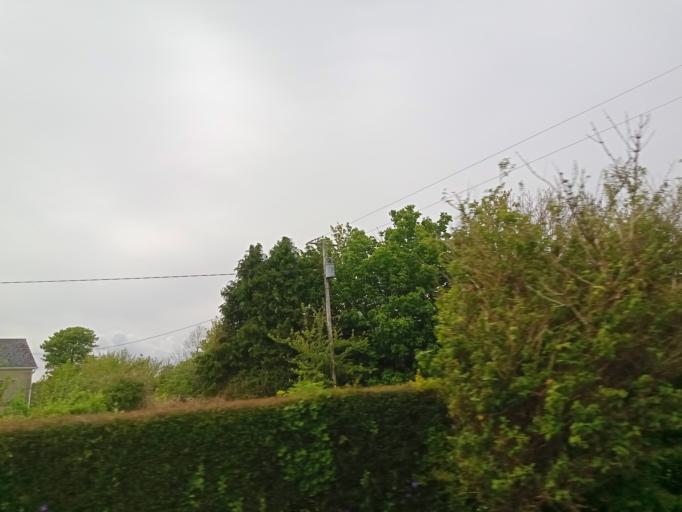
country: IE
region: Leinster
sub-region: Laois
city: Rathdowney
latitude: 52.7164
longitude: -7.4861
